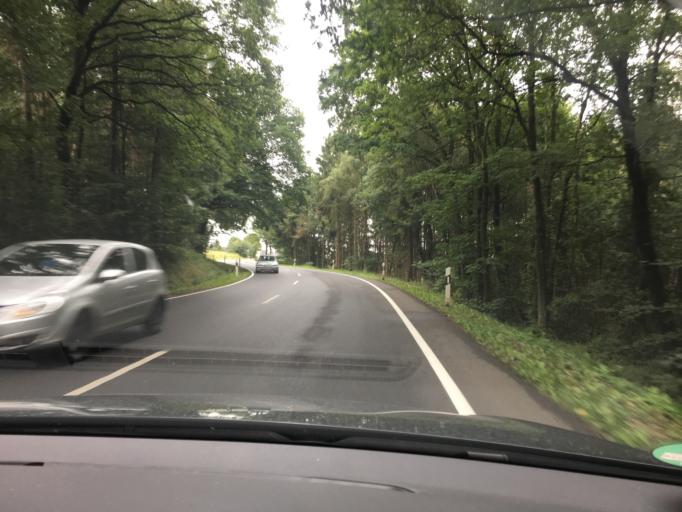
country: DE
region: North Rhine-Westphalia
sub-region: Regierungsbezirk Koln
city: Hurtgenwald
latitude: 50.7393
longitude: 6.3956
